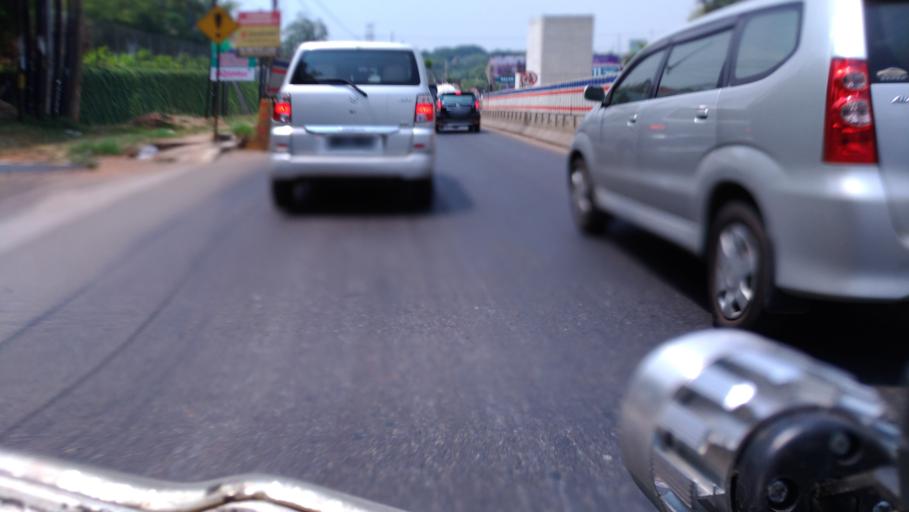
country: ID
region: West Java
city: Cileungsir
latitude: -6.3823
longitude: 106.9316
